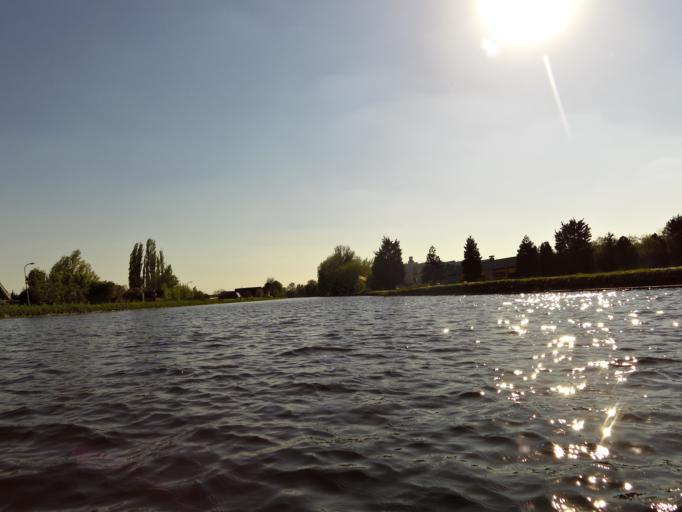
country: NL
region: South Holland
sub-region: Gemeente Voorschoten
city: Voorschoten
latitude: 52.0978
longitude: 4.4200
